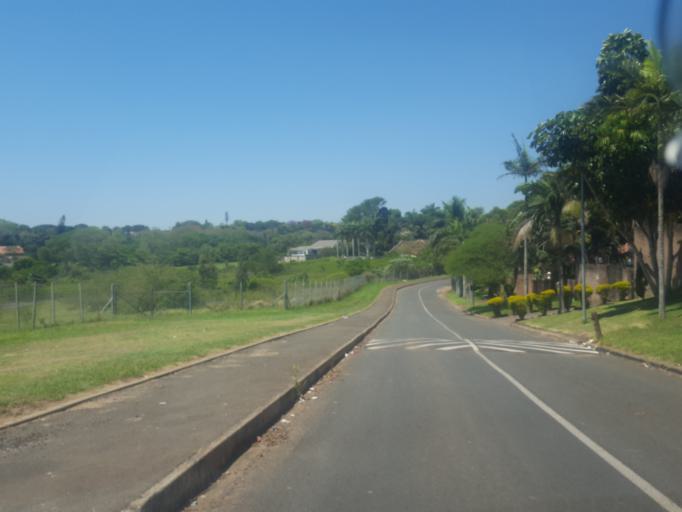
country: ZA
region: KwaZulu-Natal
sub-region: uThungulu District Municipality
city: Empangeni
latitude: -28.7425
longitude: 31.9032
